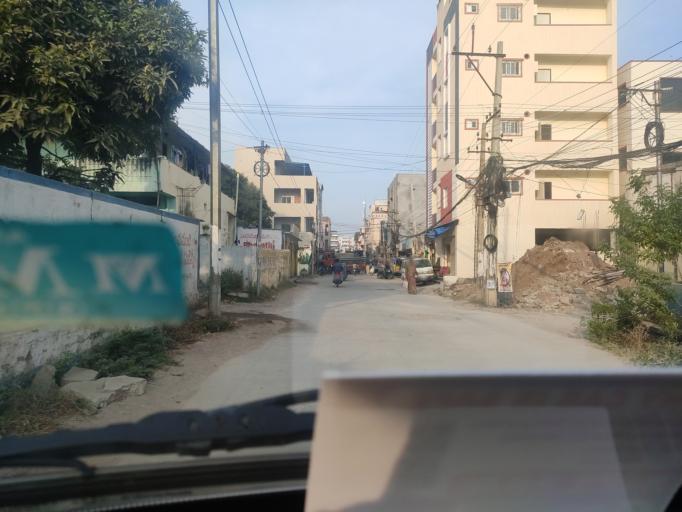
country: IN
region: Telangana
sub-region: Rangareddi
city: Kukatpalli
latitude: 17.5050
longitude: 78.4135
